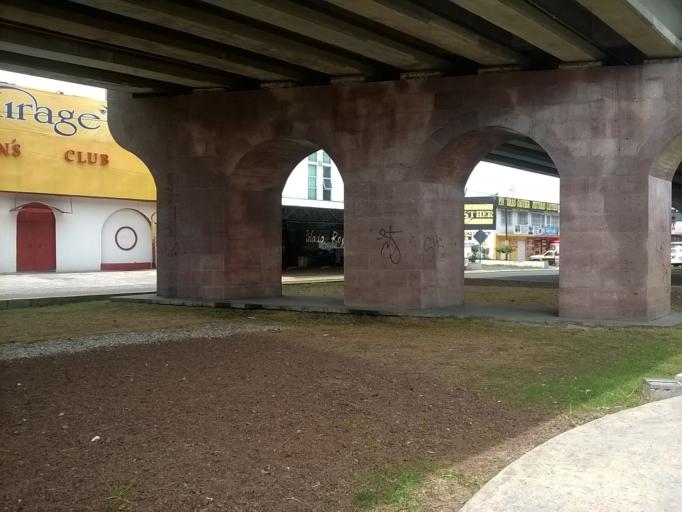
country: MX
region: Michoacan
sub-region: Tarimbaro
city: Real Hacienda (Metropolis)
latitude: 19.7268
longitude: -101.2129
